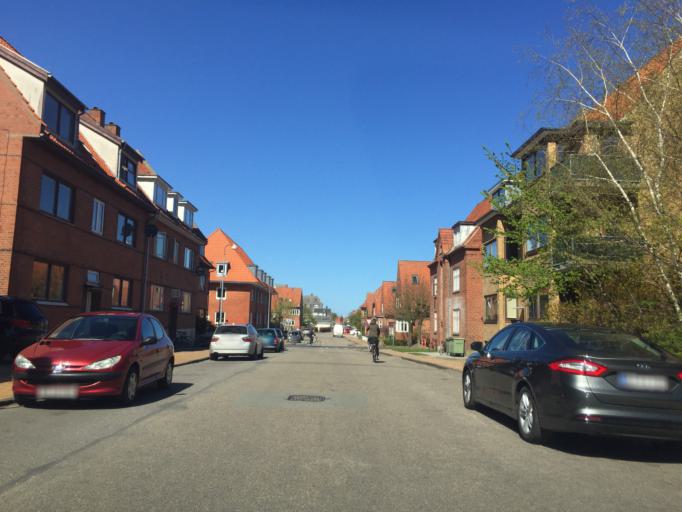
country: DK
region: South Denmark
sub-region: Odense Kommune
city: Odense
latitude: 55.4056
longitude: 10.3991
